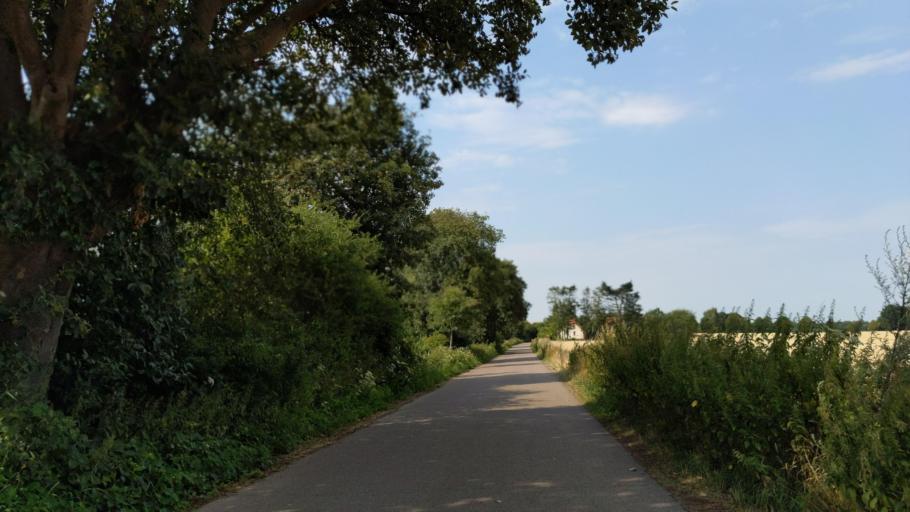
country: DE
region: Schleswig-Holstein
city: Behlendorf
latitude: 53.6942
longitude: 10.6711
